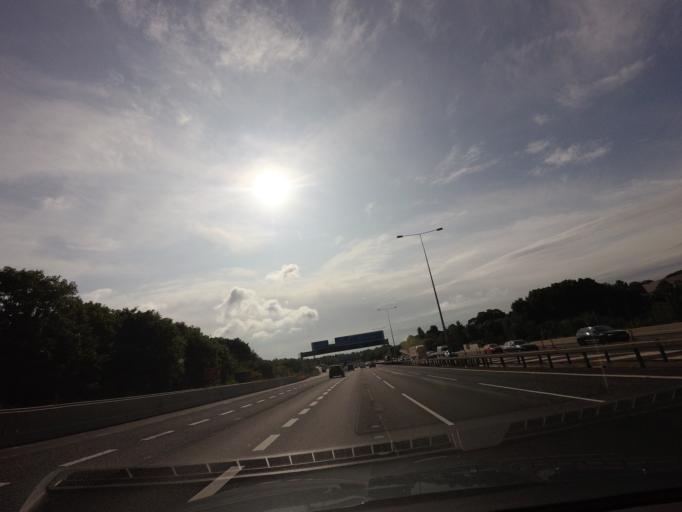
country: GB
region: England
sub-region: Kent
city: Aylesford
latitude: 51.2982
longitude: 0.4790
